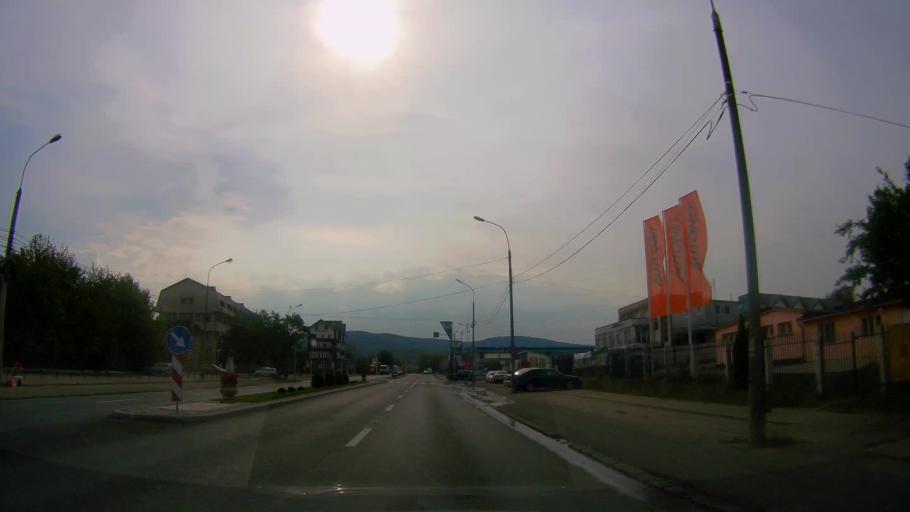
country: RO
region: Salaj
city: Zalau
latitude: 47.1991
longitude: 23.0574
